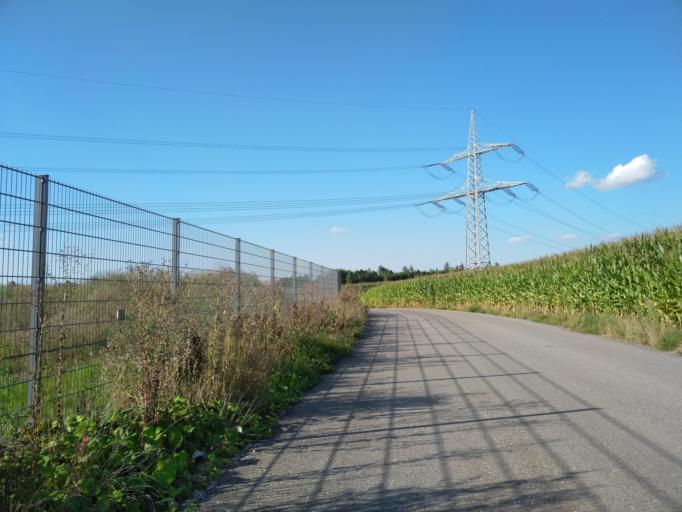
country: DE
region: Bavaria
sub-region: Swabia
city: Wasserburg
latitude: 48.4319
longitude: 10.3010
